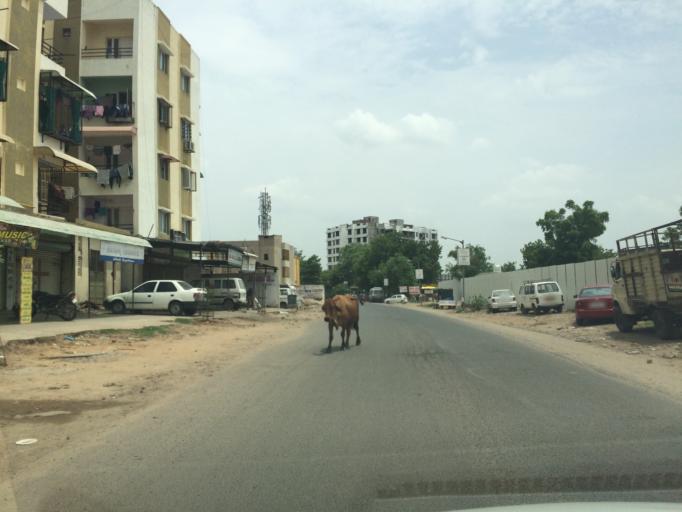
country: IN
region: Gujarat
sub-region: Ahmadabad
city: Ahmedabad
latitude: 23.0752
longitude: 72.5646
